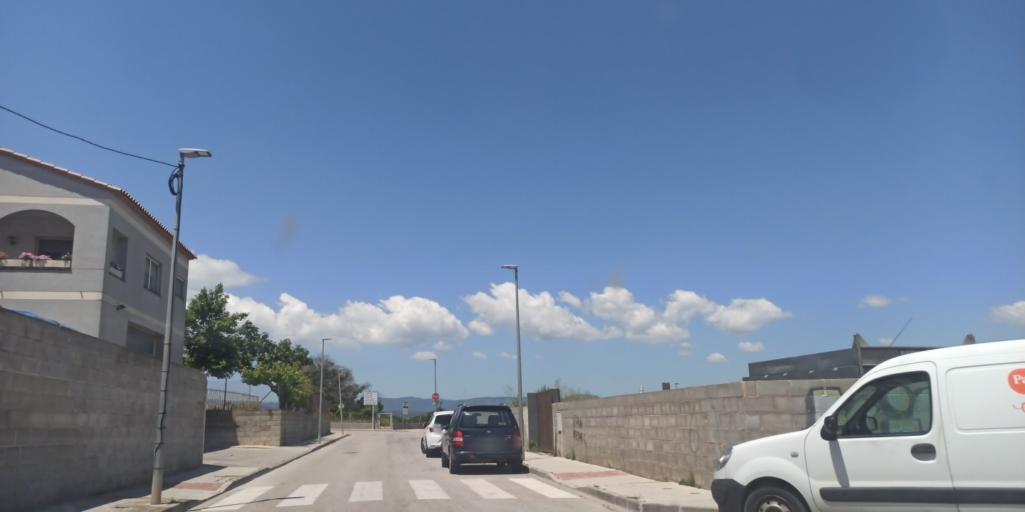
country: ES
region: Catalonia
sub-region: Provincia de Barcelona
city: Vilafranca del Penedes
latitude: 41.3271
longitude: 1.6940
